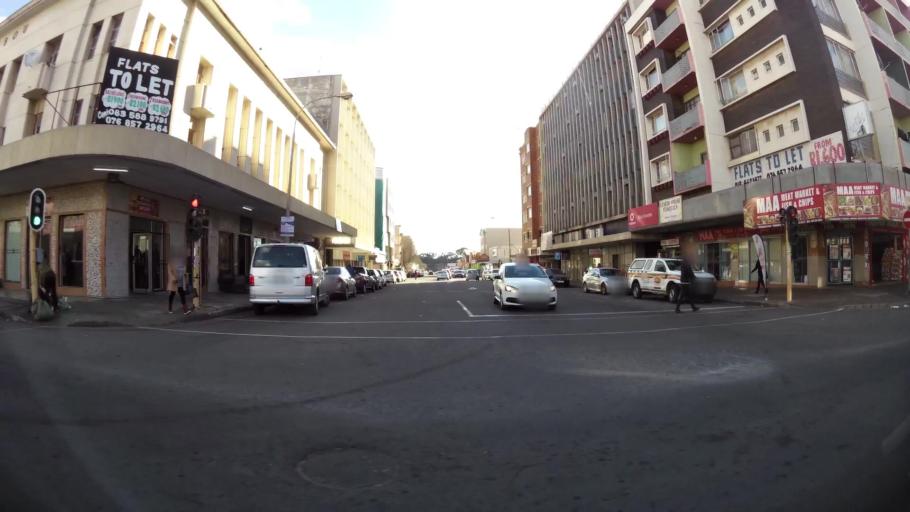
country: ZA
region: North-West
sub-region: Dr Kenneth Kaunda District Municipality
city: Klerksdorp
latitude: -26.8687
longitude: 26.6658
